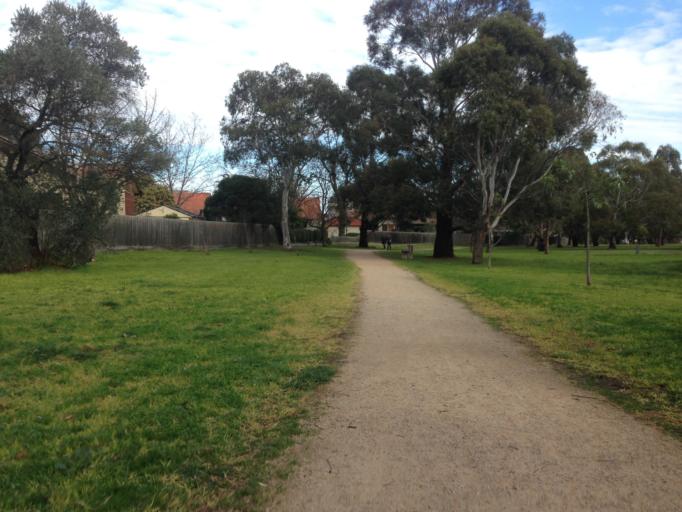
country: AU
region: Victoria
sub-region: Banyule
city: Bellfield
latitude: -37.7596
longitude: 145.0407
